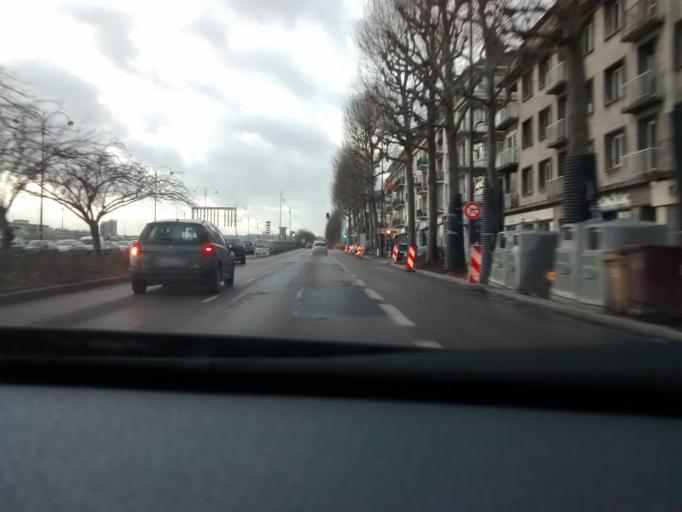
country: FR
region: Haute-Normandie
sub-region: Departement de la Seine-Maritime
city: Rouen
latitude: 49.4368
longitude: 1.0985
